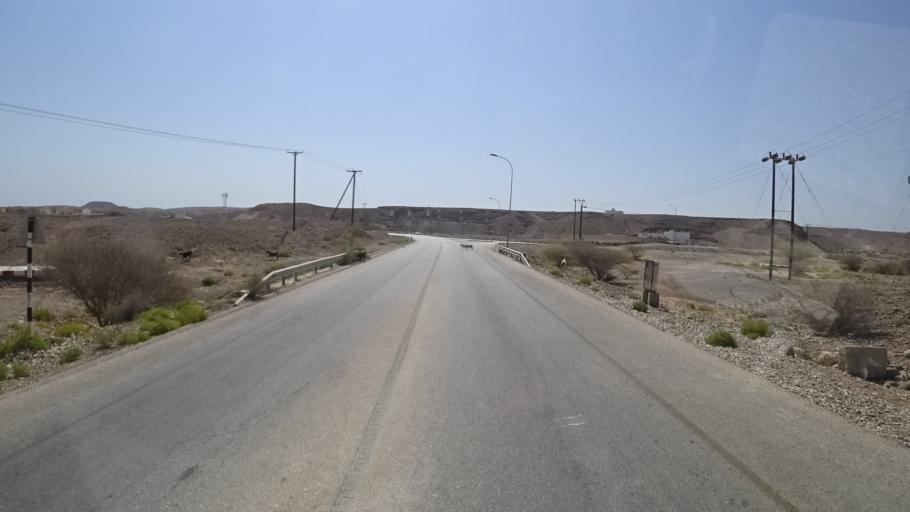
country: OM
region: Ash Sharqiyah
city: Sur
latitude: 22.5427
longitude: 59.5037
